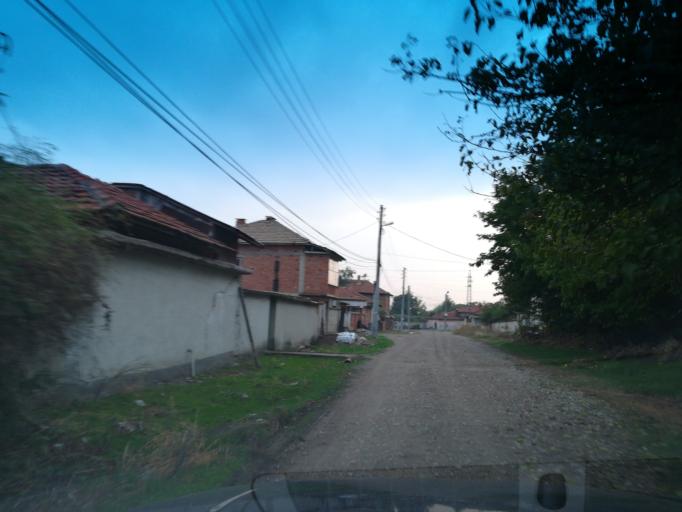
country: BG
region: Stara Zagora
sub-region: Obshtina Chirpan
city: Chirpan
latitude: 42.1729
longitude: 25.2069
